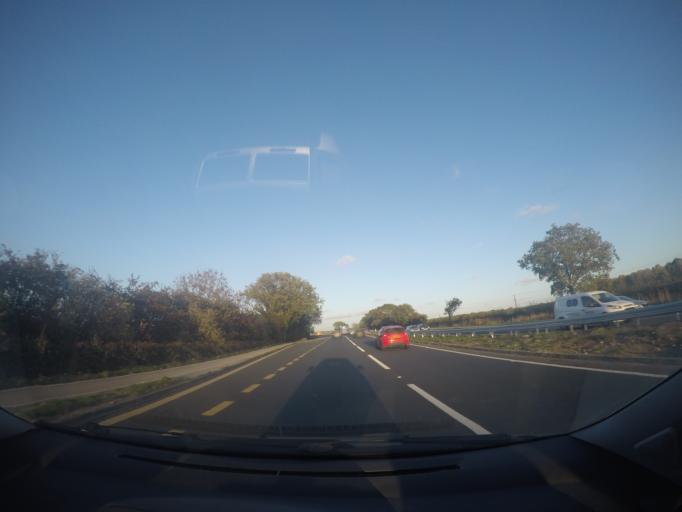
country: GB
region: England
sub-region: City of York
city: Askham Richard
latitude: 53.8937
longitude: -1.2146
